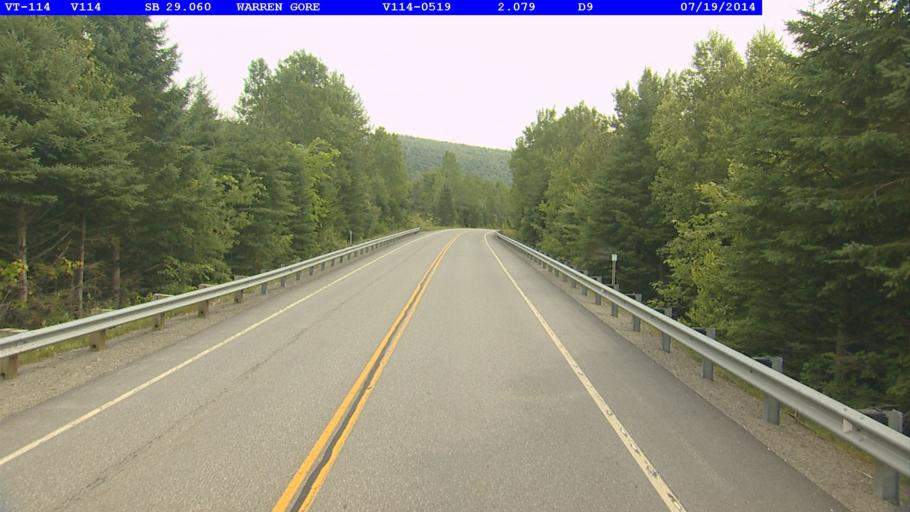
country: CA
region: Quebec
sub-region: Estrie
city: Coaticook
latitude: 44.9137
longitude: -71.8755
